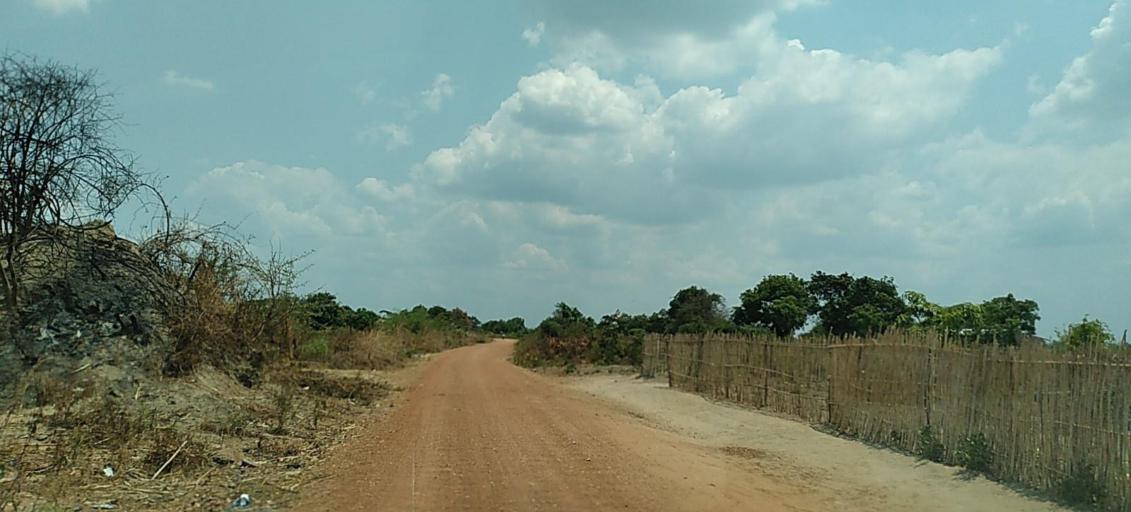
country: ZM
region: Copperbelt
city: Luanshya
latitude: -13.1332
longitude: 28.3133
